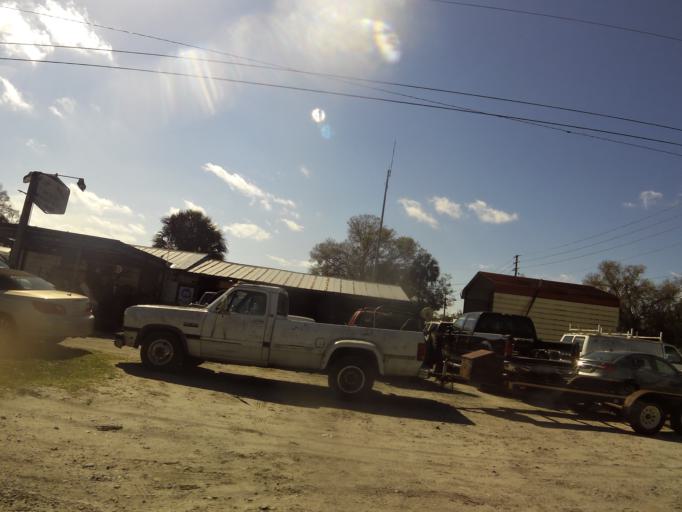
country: US
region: Florida
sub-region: Volusia County
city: Pierson
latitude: 29.1880
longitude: -81.4219
